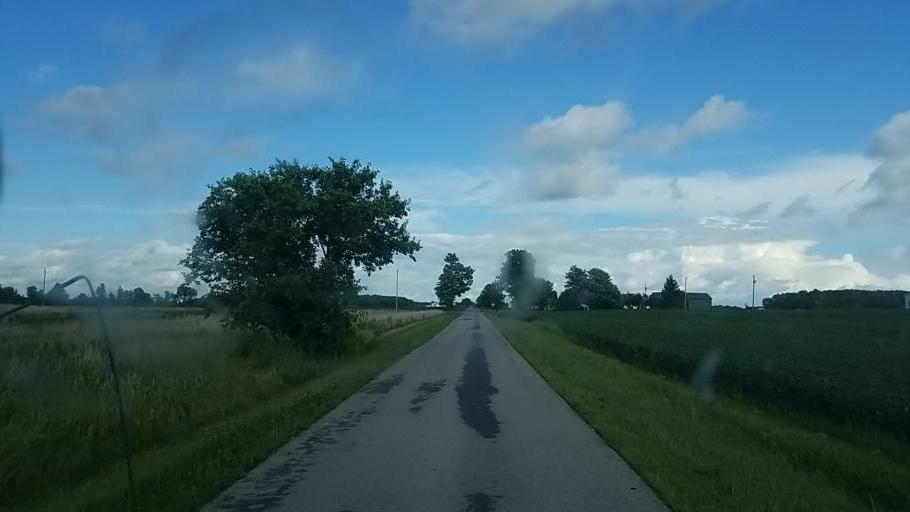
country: US
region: Ohio
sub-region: Hardin County
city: Forest
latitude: 40.7596
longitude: -83.4604
